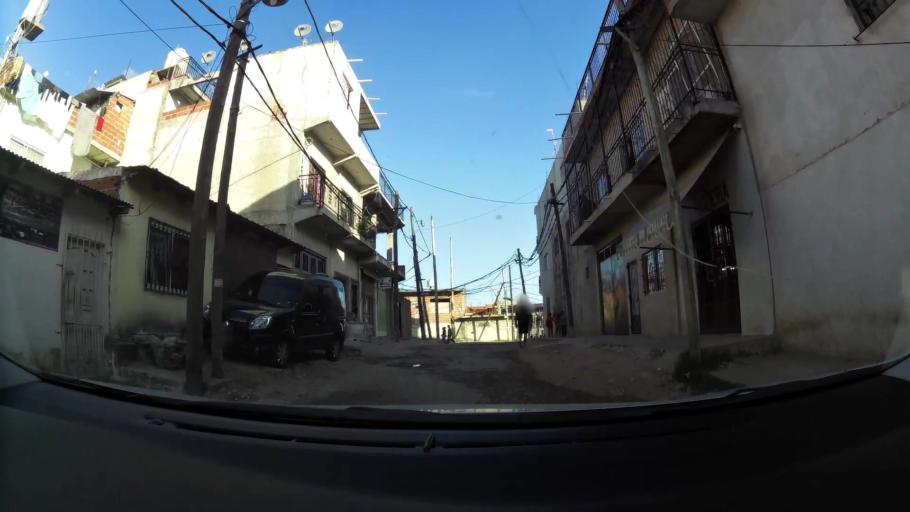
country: AR
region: Buenos Aires F.D.
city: Villa Lugano
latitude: -34.7076
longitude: -58.4827
